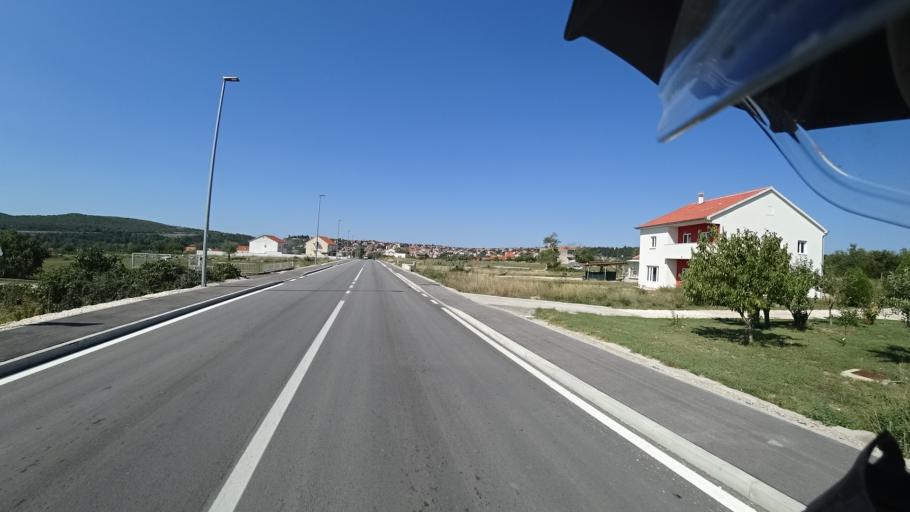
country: HR
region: Sibensko-Kniniska
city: Drnis
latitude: 43.8630
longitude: 16.1712
